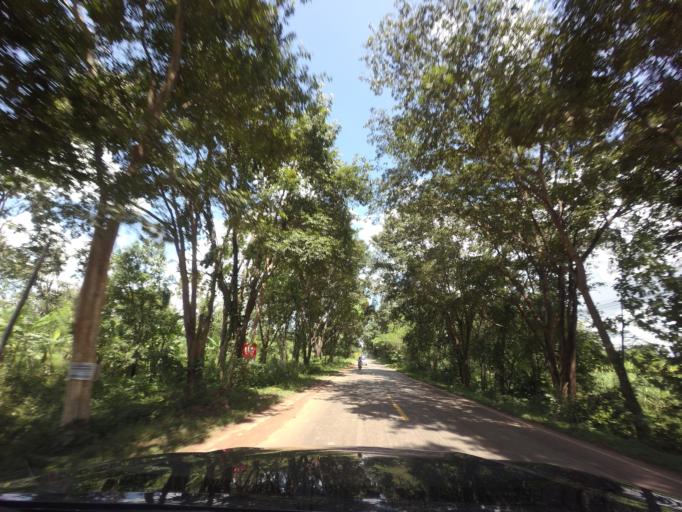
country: TH
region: Changwat Udon Thani
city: Ban Dung
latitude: 17.6639
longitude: 103.1574
